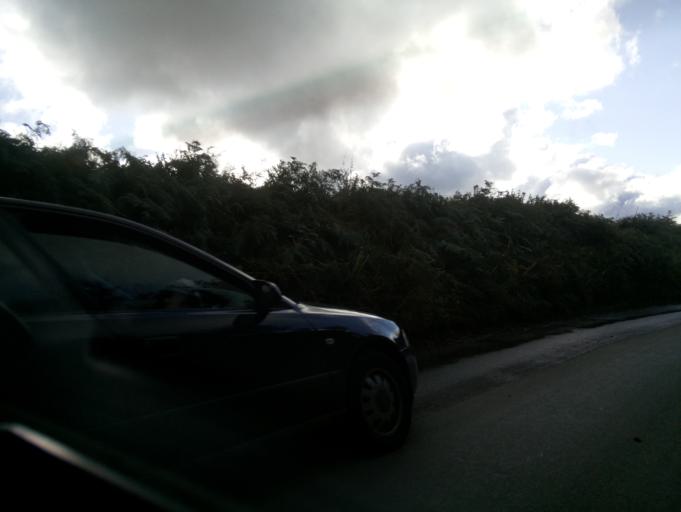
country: GB
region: England
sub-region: Devon
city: South Brent
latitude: 50.3790
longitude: -3.7623
